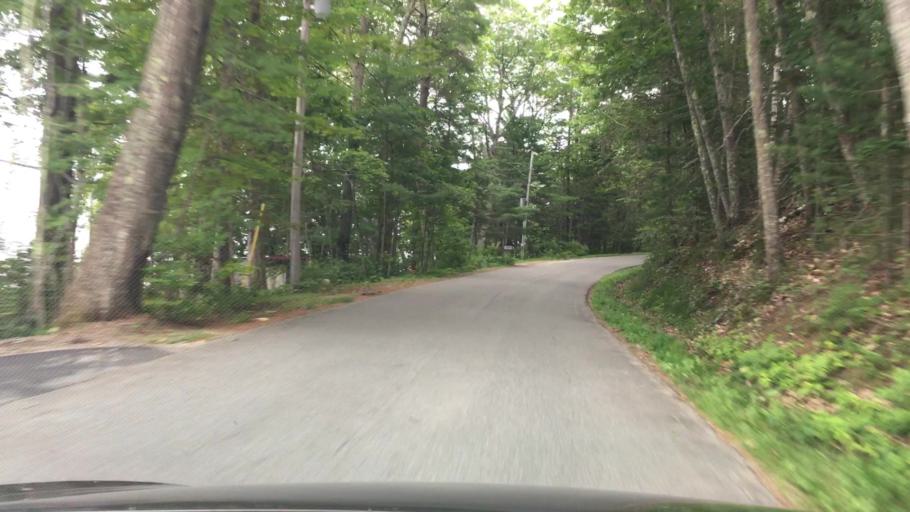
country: US
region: Maine
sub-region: Waldo County
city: Stockton Springs
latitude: 44.5127
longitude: -68.8112
